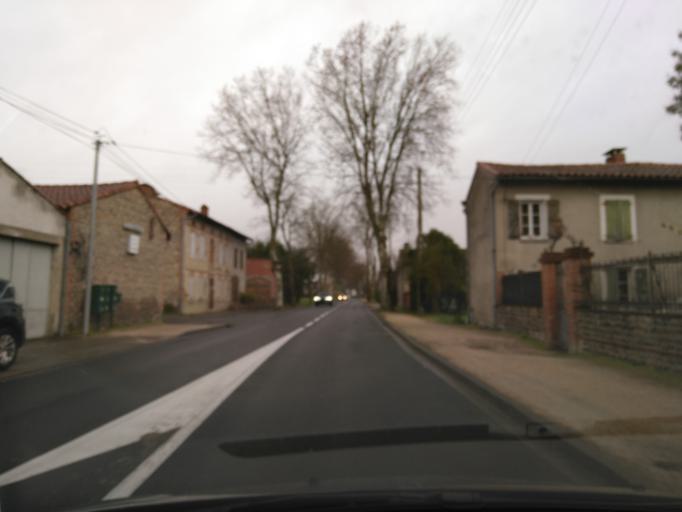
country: FR
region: Midi-Pyrenees
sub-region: Departement de la Haute-Garonne
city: Carbonne
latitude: 43.2984
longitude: 1.2195
